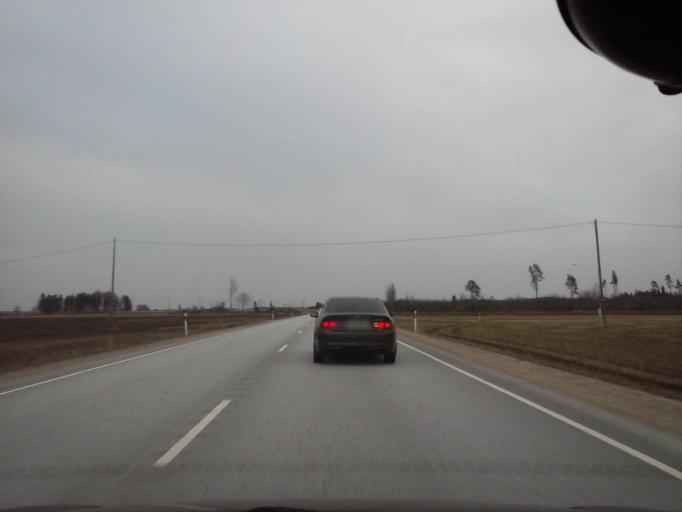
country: EE
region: Jogevamaa
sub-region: Poltsamaa linn
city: Poltsamaa
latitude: 58.7268
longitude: 25.8553
